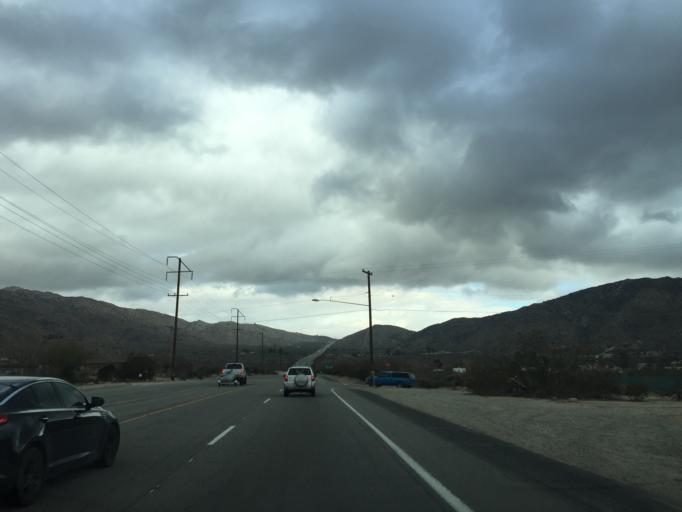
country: US
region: California
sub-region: San Bernardino County
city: Morongo Valley
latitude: 34.0889
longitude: -116.5205
